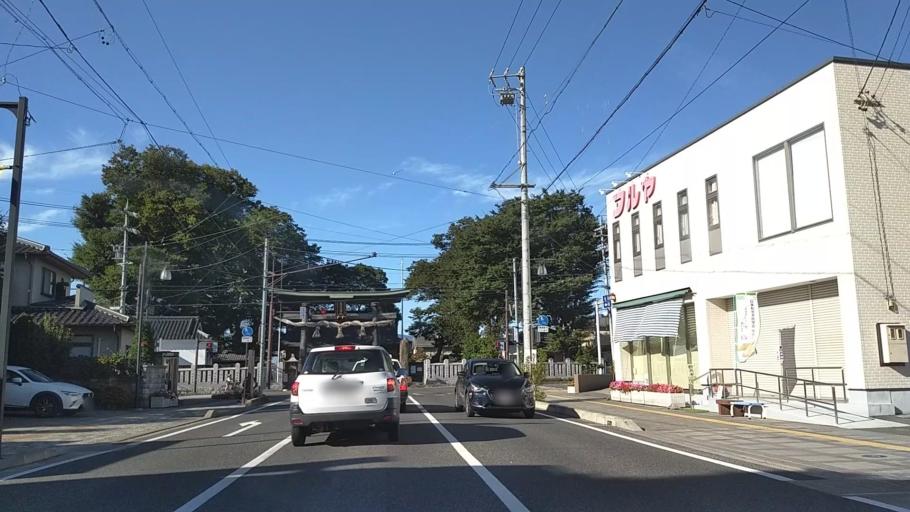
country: JP
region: Nagano
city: Nagano-shi
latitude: 36.5383
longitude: 138.1265
